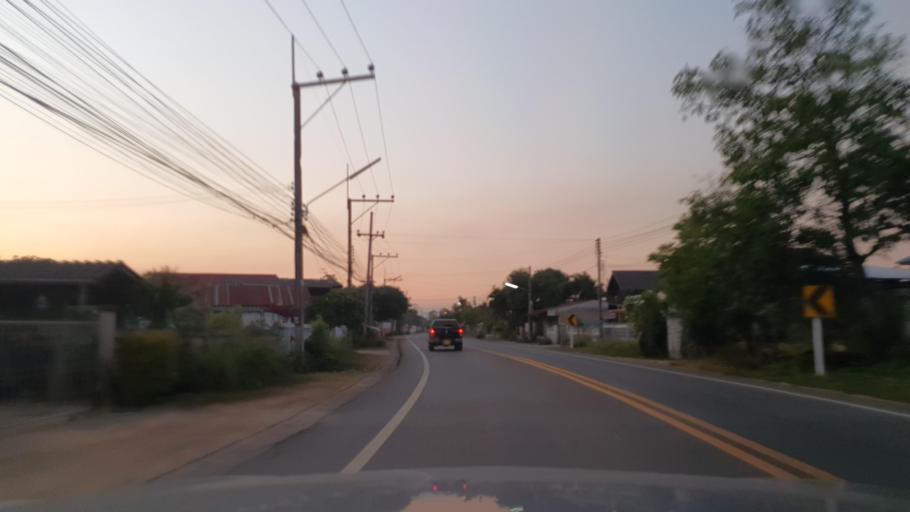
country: TH
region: Phayao
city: Dok Kham Tai
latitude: 19.1400
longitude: 100.0184
